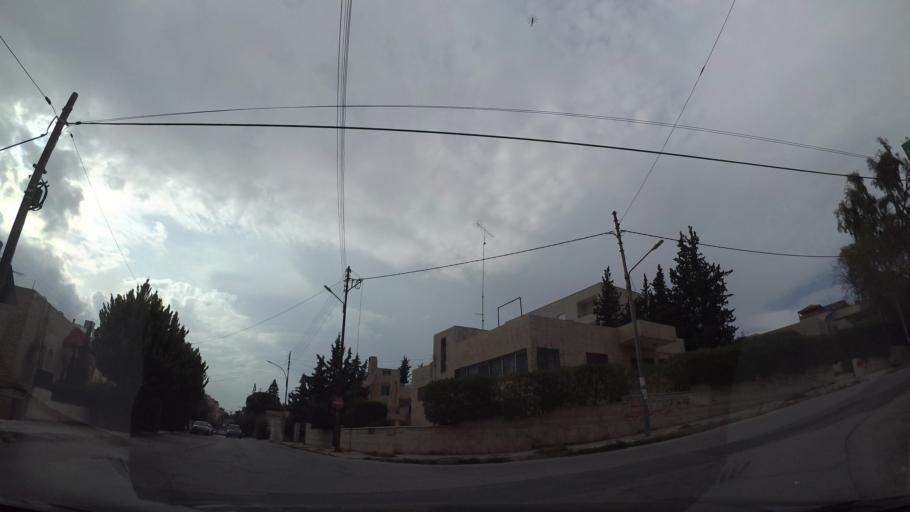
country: JO
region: Amman
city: Amman
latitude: 32.0040
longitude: 35.9472
